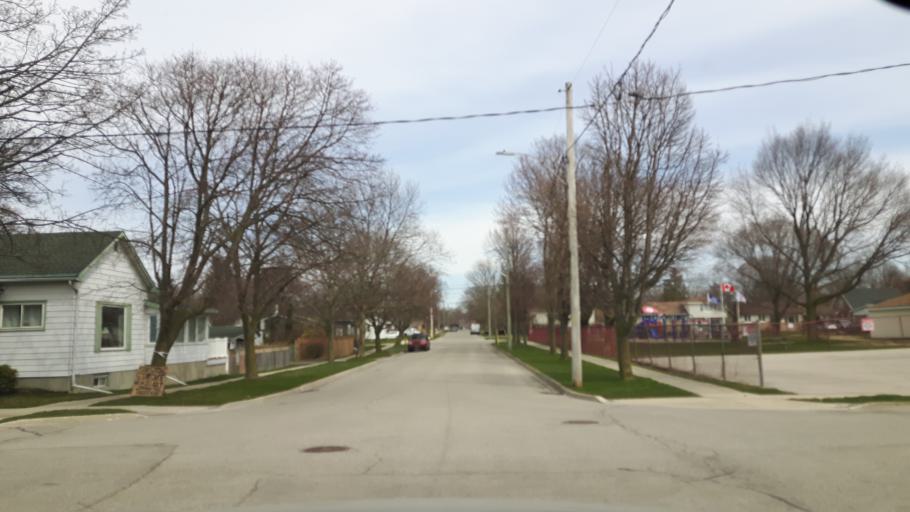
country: CA
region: Ontario
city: Goderich
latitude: 43.7371
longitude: -81.7126
